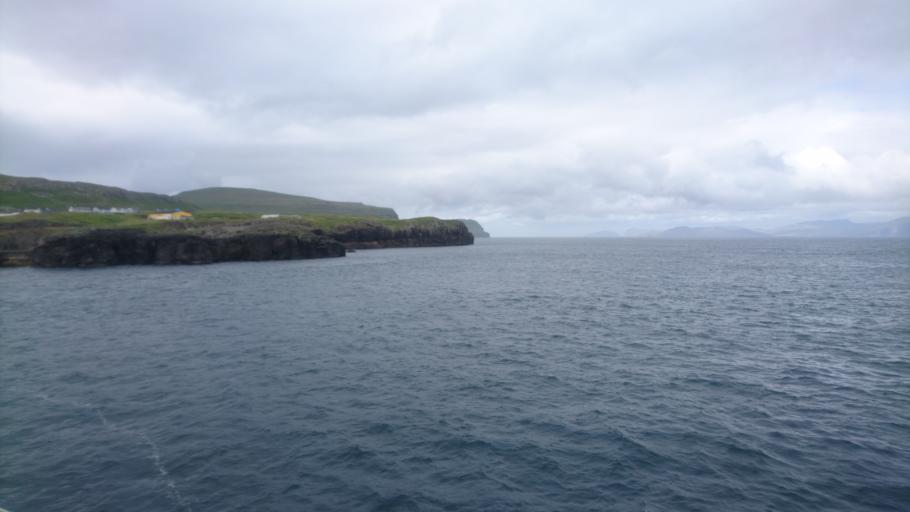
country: FO
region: Sandoy
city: Sandur
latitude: 61.9063
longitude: -6.8755
